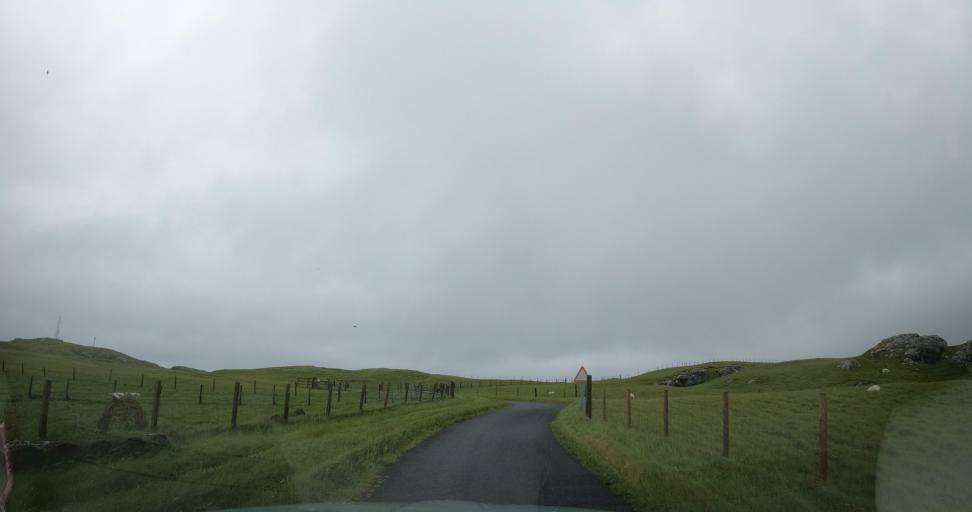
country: GB
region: Scotland
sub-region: Eilean Siar
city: Barra
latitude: 57.0060
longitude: -7.4994
